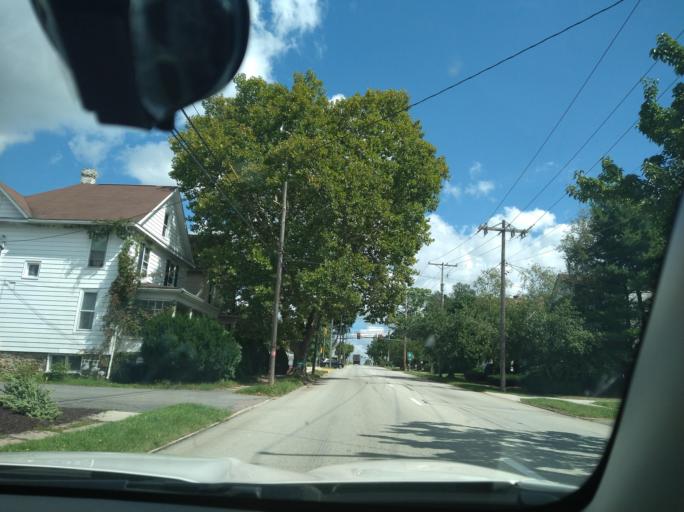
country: US
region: Pennsylvania
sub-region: Somerset County
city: Somerset
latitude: 40.0075
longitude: -79.0839
